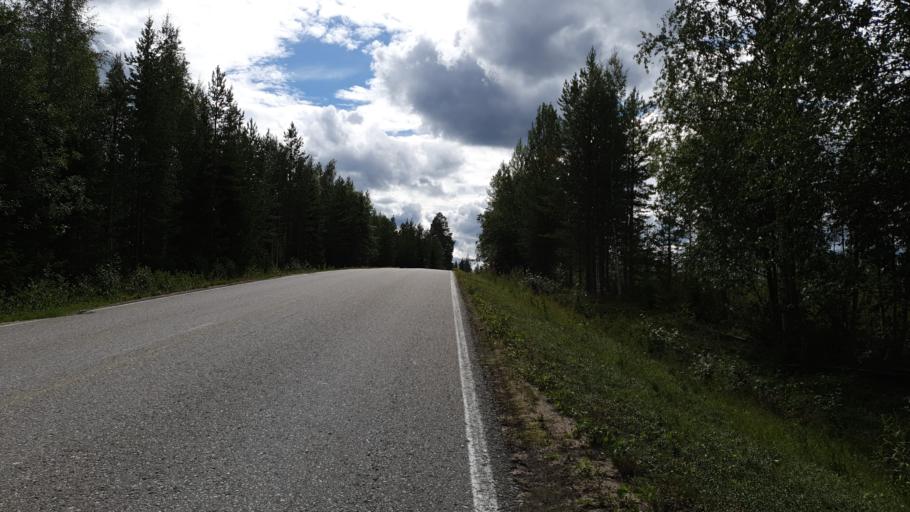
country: FI
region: Kainuu
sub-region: Kehys-Kainuu
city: Kuhmo
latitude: 64.4237
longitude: 29.8153
